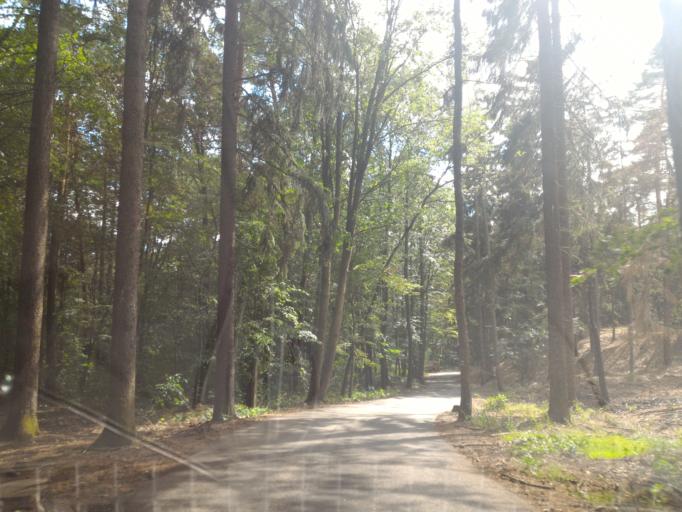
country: CZ
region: Central Bohemia
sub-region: Okres Kutna Hora
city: Kutna Hora
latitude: 49.9706
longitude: 15.2825
